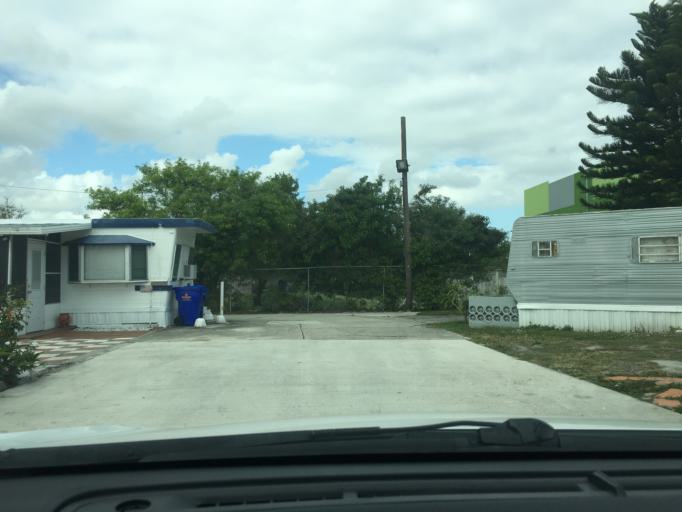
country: US
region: Florida
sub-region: Broward County
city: Dania Beach
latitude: 26.0645
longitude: -80.1717
